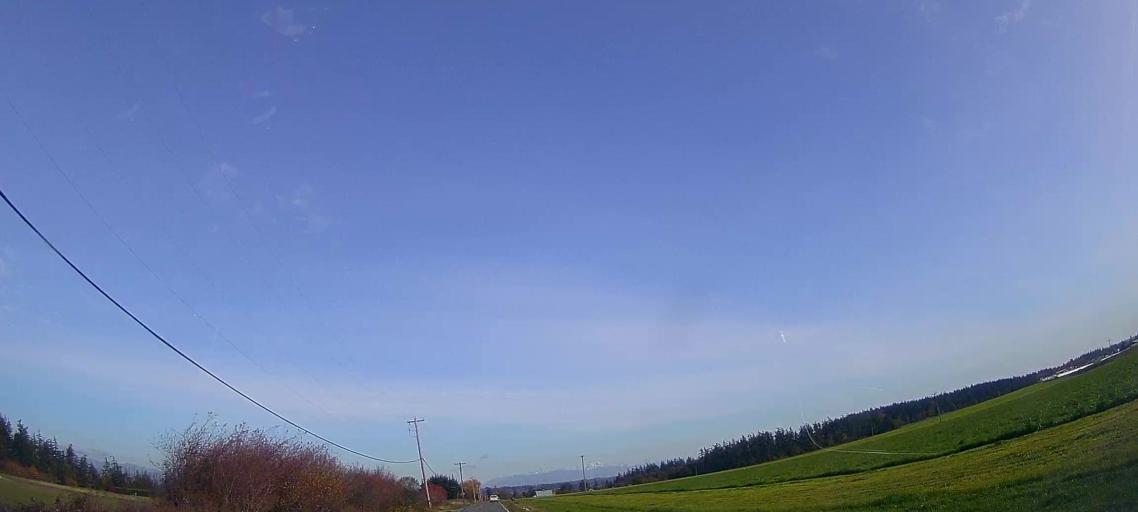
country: US
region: Washington
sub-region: Snohomish County
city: Stanwood
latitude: 48.2544
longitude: -122.4357
